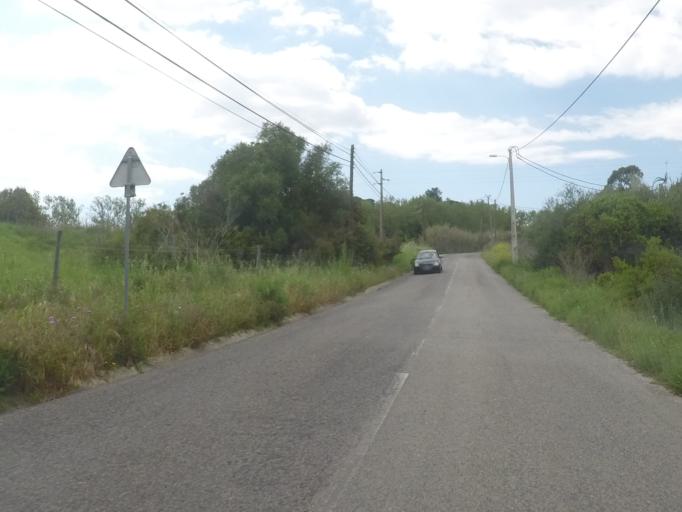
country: PT
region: Setubal
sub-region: Palmela
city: Quinta do Anjo
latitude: 38.5064
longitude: -9.0001
